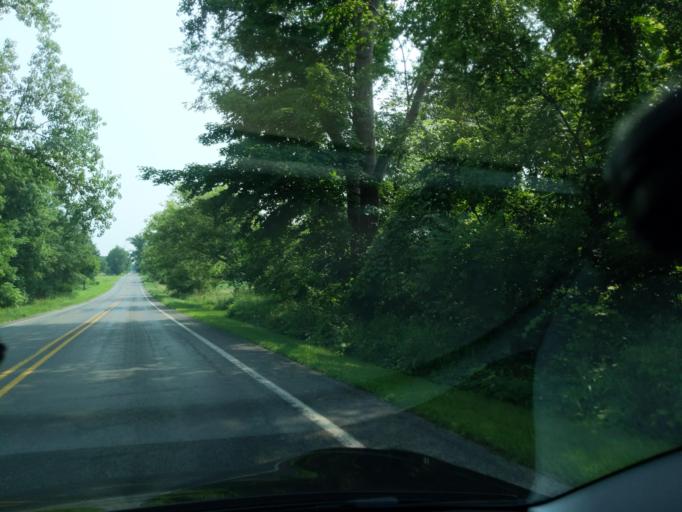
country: US
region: Michigan
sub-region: Eaton County
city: Eaton Rapids
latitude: 42.4758
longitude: -84.5609
